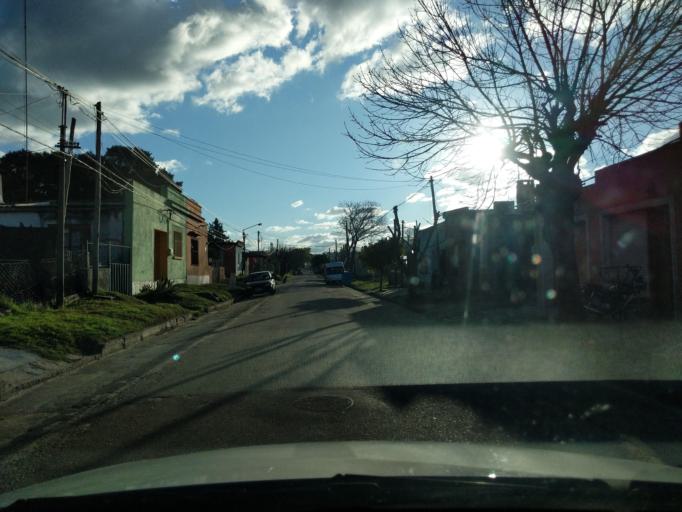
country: UY
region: Florida
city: Florida
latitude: -34.1009
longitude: -56.2259
